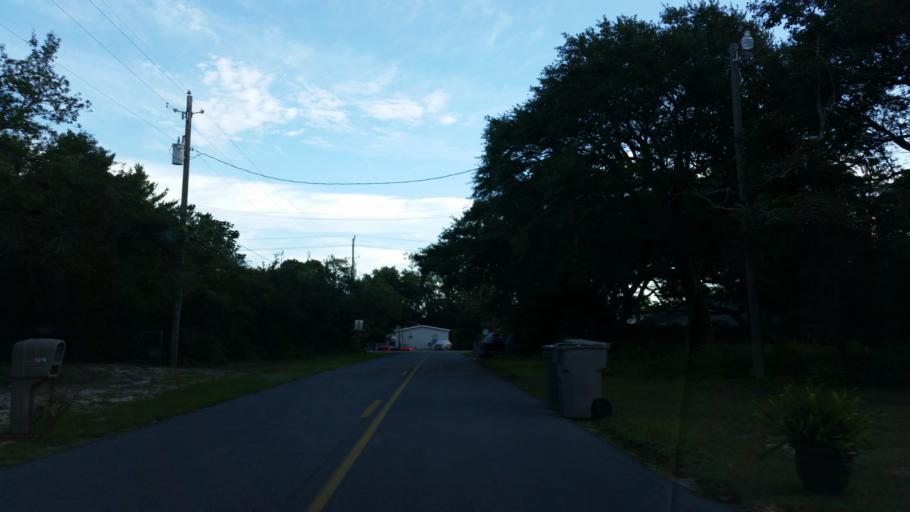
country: US
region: Alabama
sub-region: Baldwin County
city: Orange Beach
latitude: 30.3155
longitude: -87.4379
